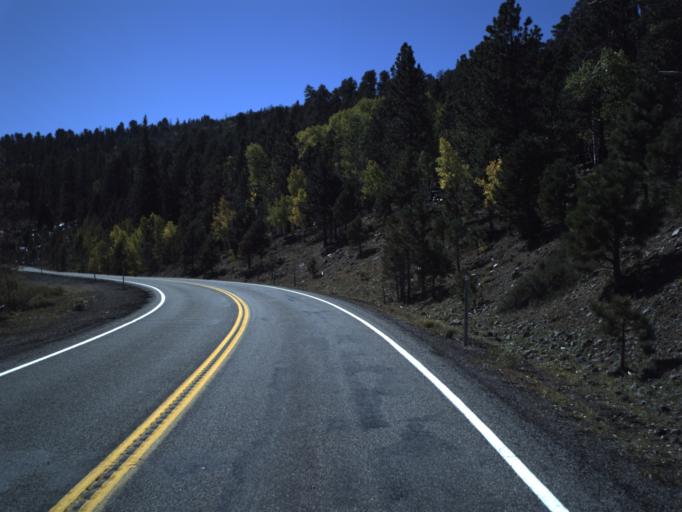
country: US
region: Utah
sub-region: Wayne County
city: Loa
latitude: 38.1552
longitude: -111.3333
